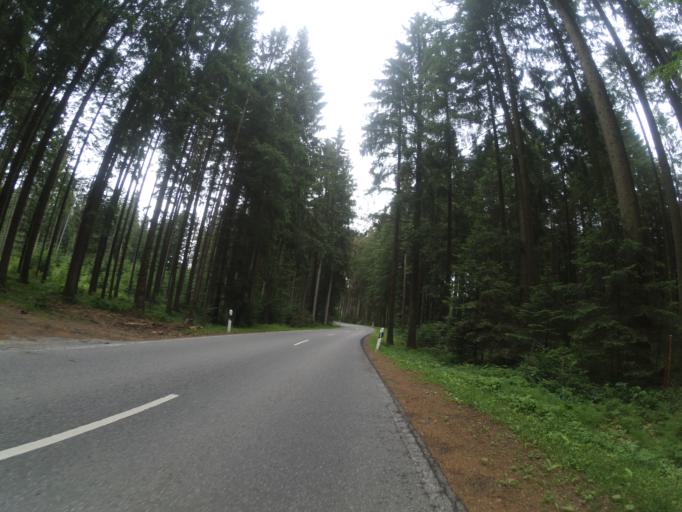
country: DE
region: Bavaria
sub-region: Swabia
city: Gestratz
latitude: 47.6981
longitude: 9.9737
